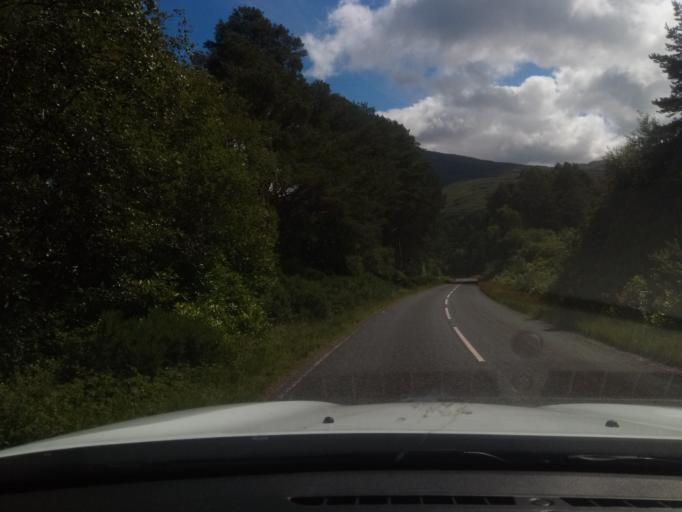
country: GB
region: Scotland
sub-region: Argyll and Bute
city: Isle Of Mull
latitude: 56.8432
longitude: -5.7522
